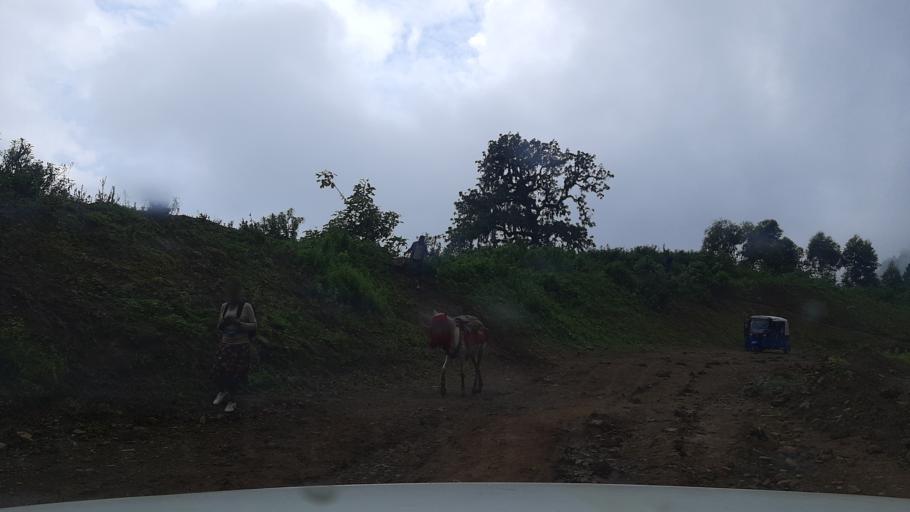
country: ET
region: Southern Nations, Nationalities, and People's Region
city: Bonga
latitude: 7.1108
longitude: 36.5284
